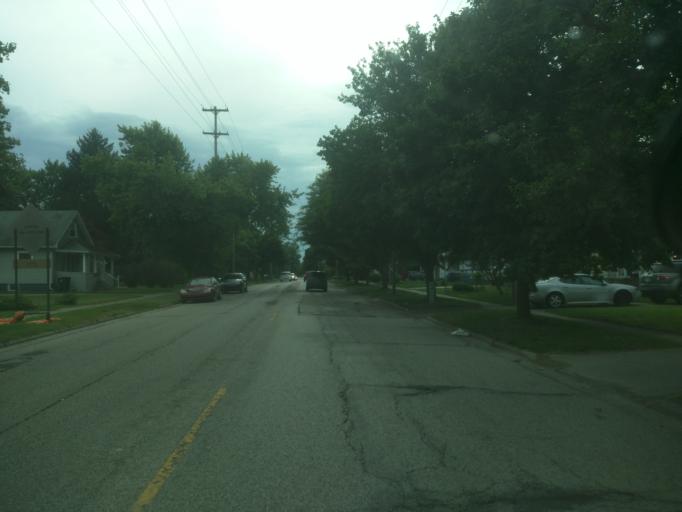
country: US
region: Michigan
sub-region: Ingham County
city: Lansing
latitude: 42.6902
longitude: -84.5414
